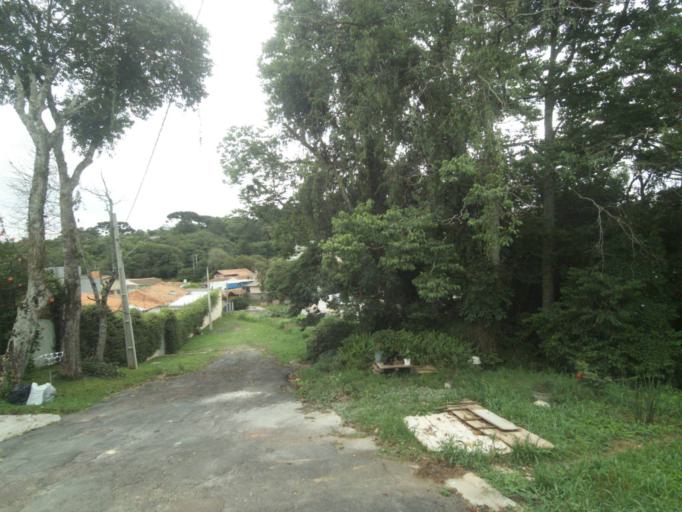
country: BR
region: Parana
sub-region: Curitiba
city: Curitiba
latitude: -25.3999
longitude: -49.2935
